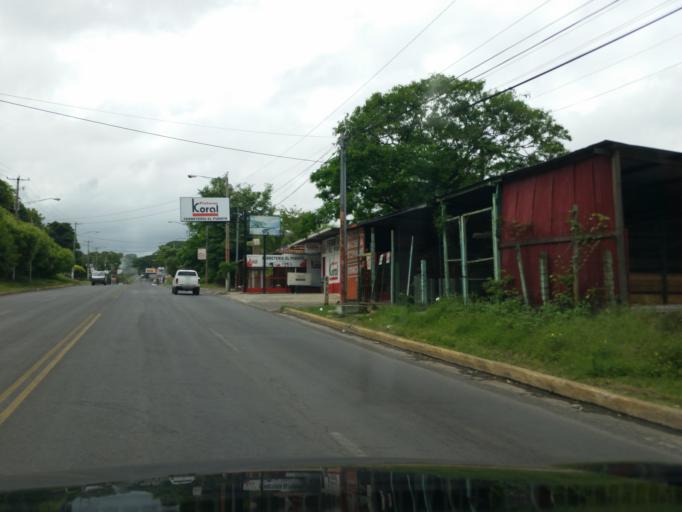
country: NI
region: Managua
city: Ciudad Sandino
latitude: 12.0764
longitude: -86.3240
